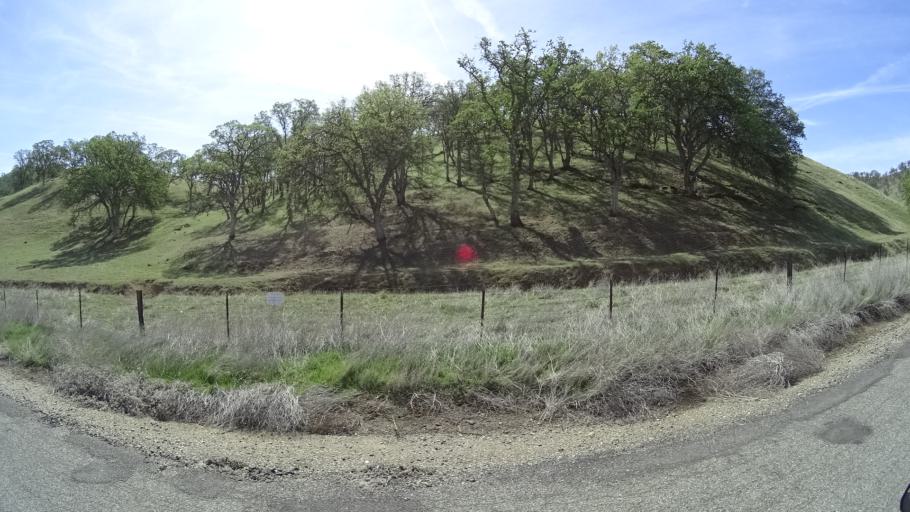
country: US
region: California
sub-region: Glenn County
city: Willows
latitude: 39.5442
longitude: -122.4081
